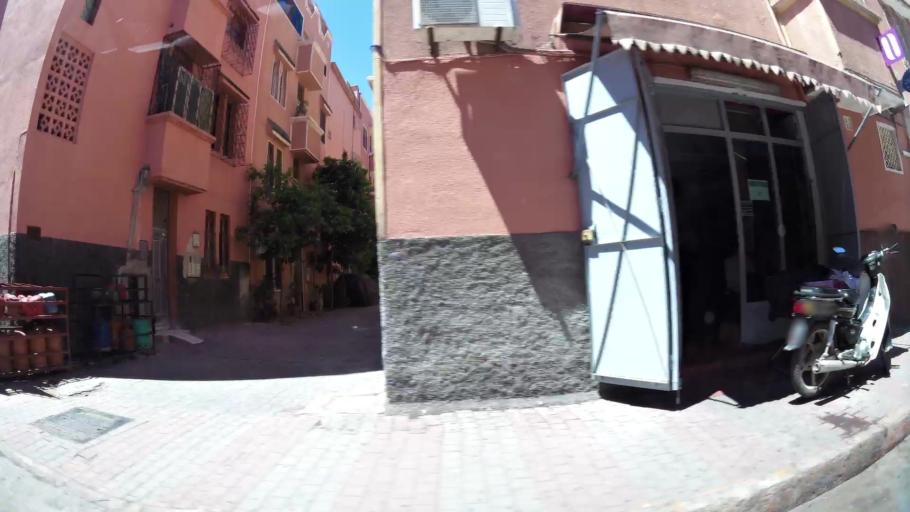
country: MA
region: Marrakech-Tensift-Al Haouz
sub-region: Marrakech
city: Marrakesh
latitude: 31.6291
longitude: -8.0525
